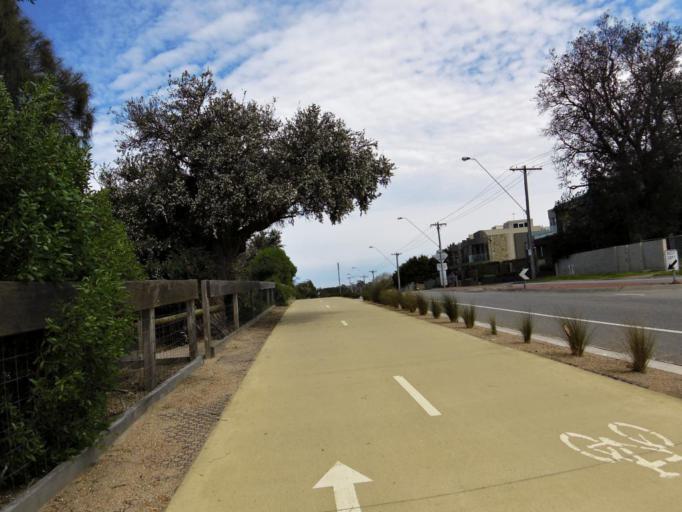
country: AU
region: Victoria
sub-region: Kingston
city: Mentone
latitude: -37.9864
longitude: 145.0511
